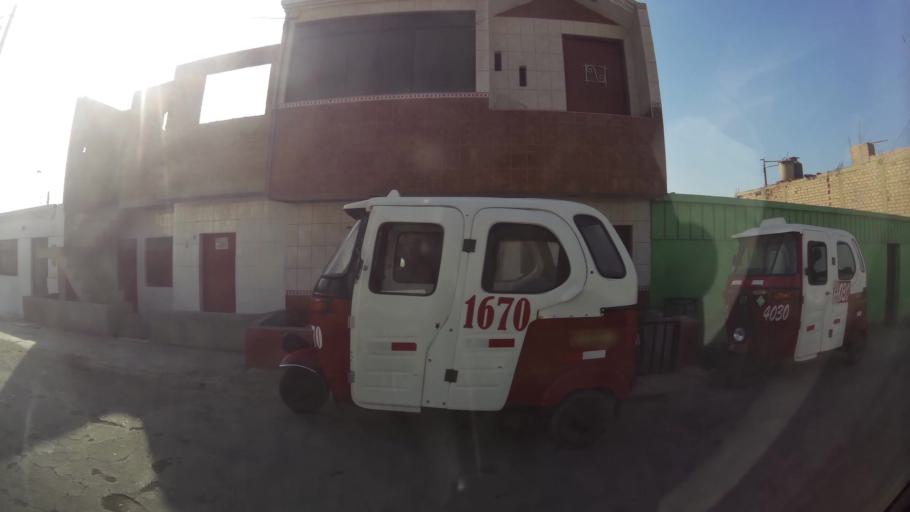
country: PE
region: Lima
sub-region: Huaura
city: Huacho
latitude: -11.1263
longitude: -77.6122
